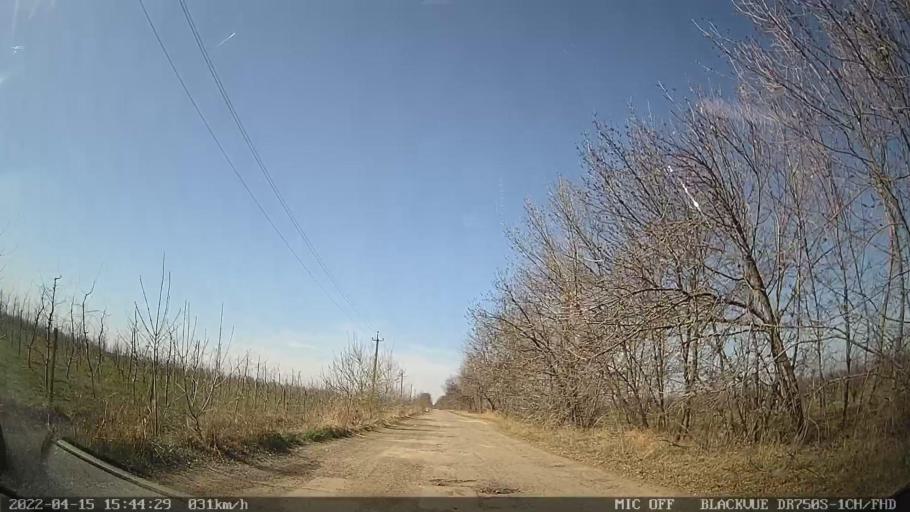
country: MD
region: Raionul Ocnita
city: Otaci
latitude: 48.3707
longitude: 27.9222
